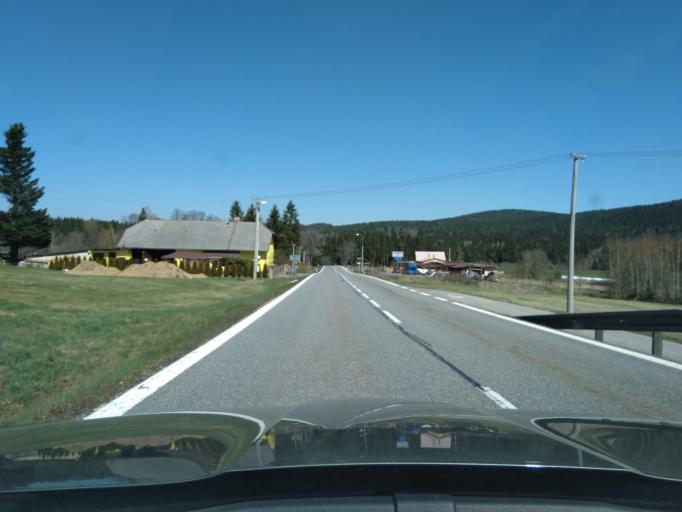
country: CZ
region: Jihocesky
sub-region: Okres Prachatice
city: Vimperk
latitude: 49.0141
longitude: 13.7687
